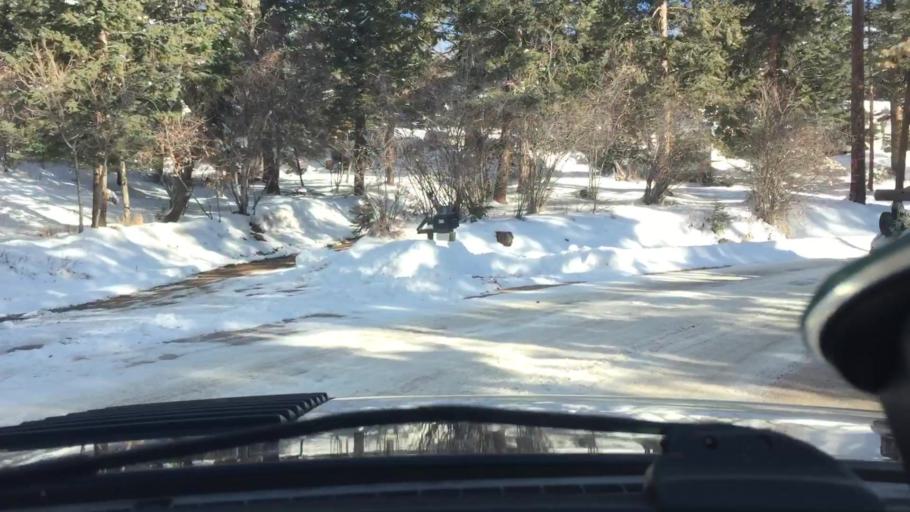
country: US
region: Colorado
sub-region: Jefferson County
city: Indian Hills
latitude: 39.5581
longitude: -105.2477
